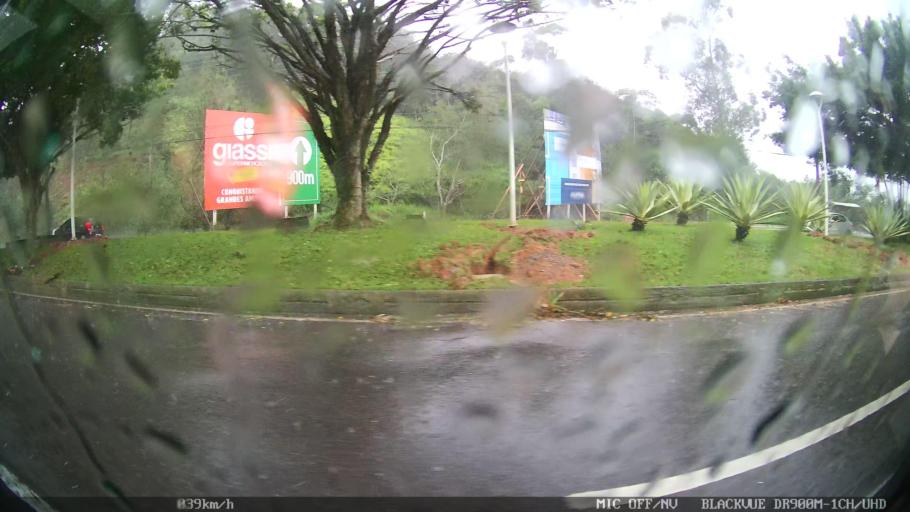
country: BR
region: Santa Catarina
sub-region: Itajai
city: Itajai
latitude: -26.9382
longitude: -48.6419
